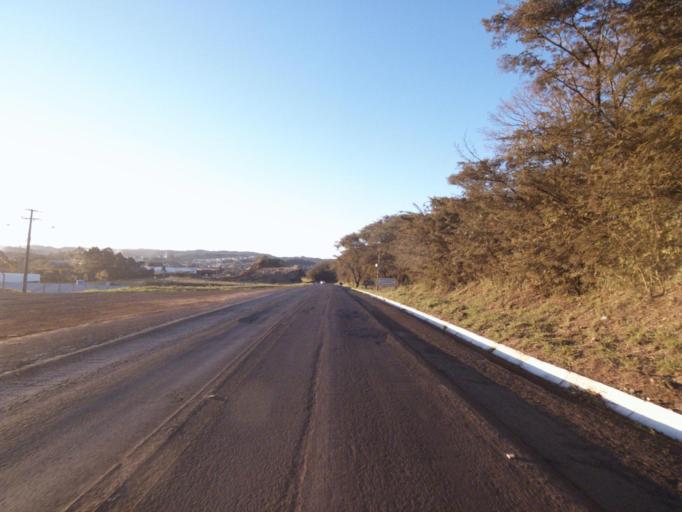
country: BR
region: Santa Catarina
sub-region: Sao Lourenco Do Oeste
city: Sao Lourenco dOeste
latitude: -26.7905
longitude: -53.1947
